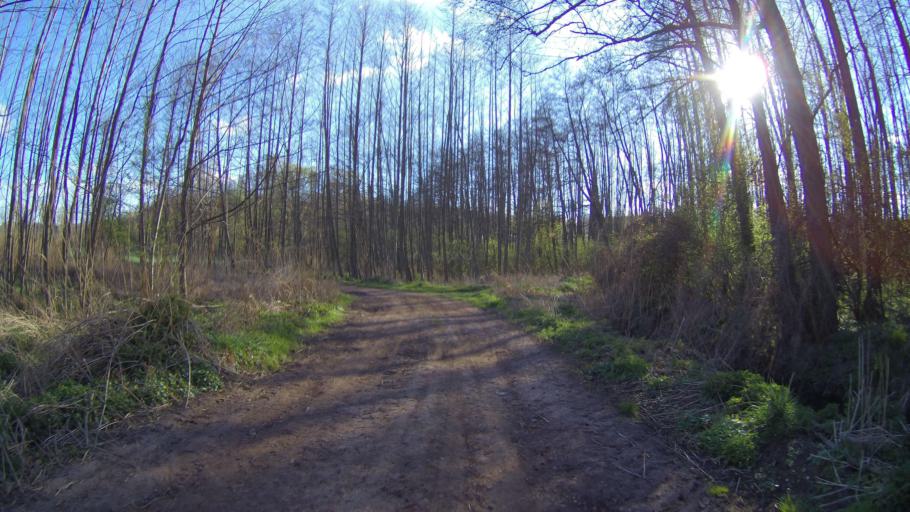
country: CZ
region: Ustecky
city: Zatec
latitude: 50.3333
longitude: 13.5892
